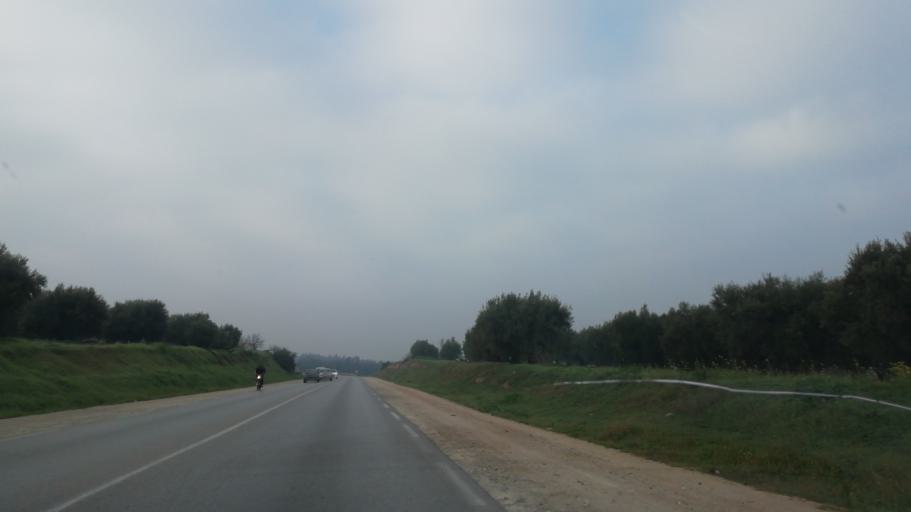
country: DZ
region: Relizane
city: Djidiouia
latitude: 35.9373
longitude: 0.8548
